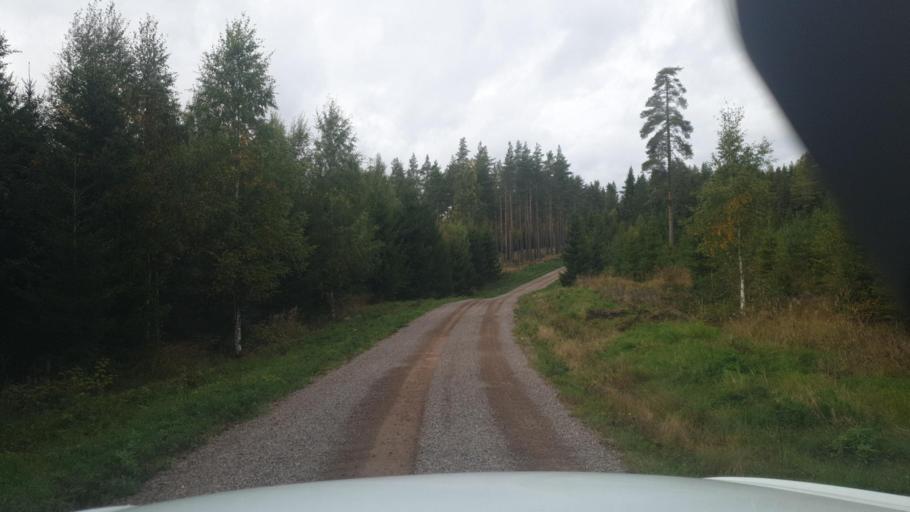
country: SE
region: Vaermland
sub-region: Torsby Kommun
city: Torsby
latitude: 59.9471
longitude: 12.7922
